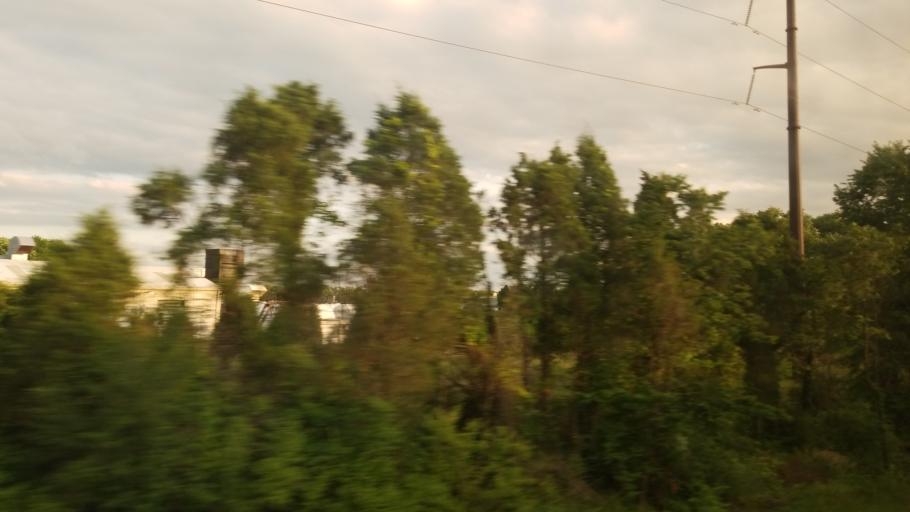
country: US
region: Virginia
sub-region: City of Manassas
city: Manassas
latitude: 38.7451
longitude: -77.4975
